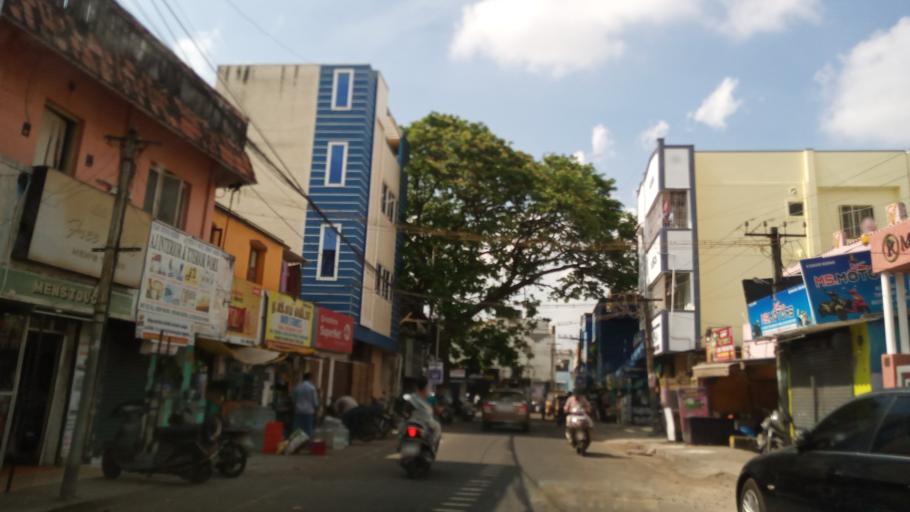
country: IN
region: Tamil Nadu
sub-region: Kancheepuram
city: Saint Thomas Mount
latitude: 12.9871
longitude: 80.1882
